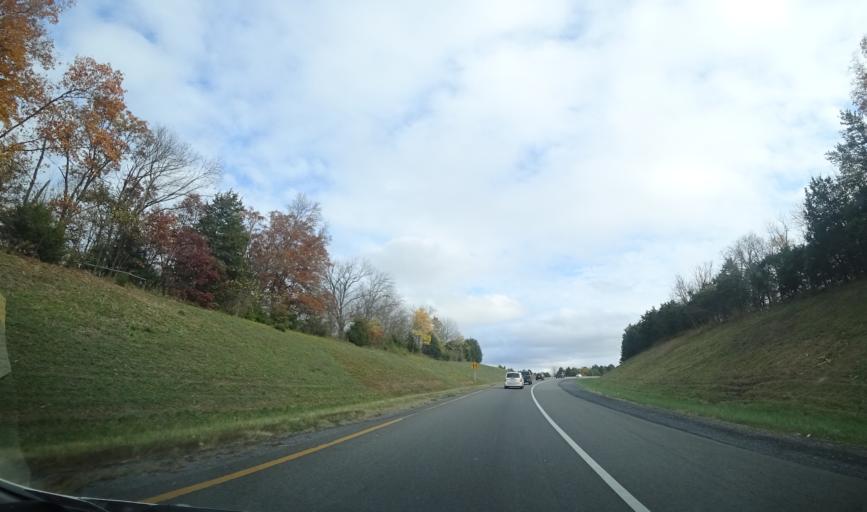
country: US
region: Virginia
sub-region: Frederick County
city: Middletown
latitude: 39.0085
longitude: -78.2986
